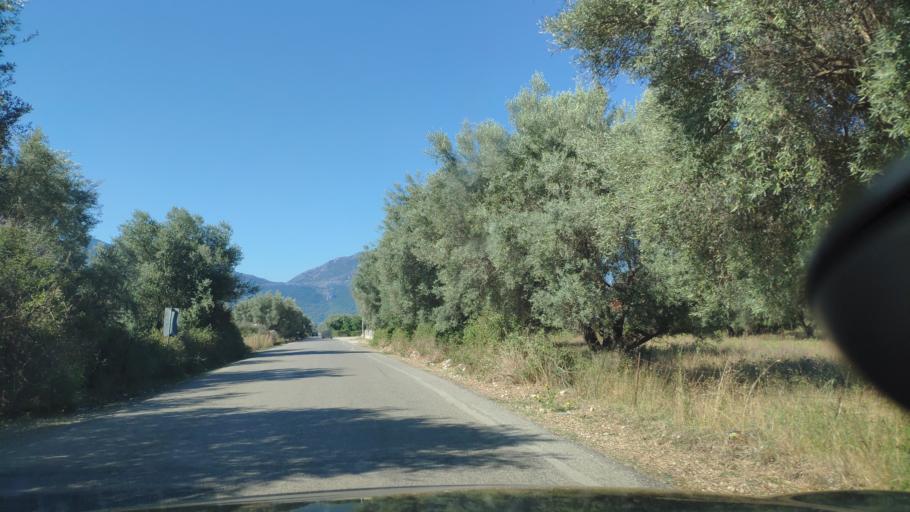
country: GR
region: West Greece
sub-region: Nomos Aitolias kai Akarnanias
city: Kandila
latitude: 38.6954
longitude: 20.9473
